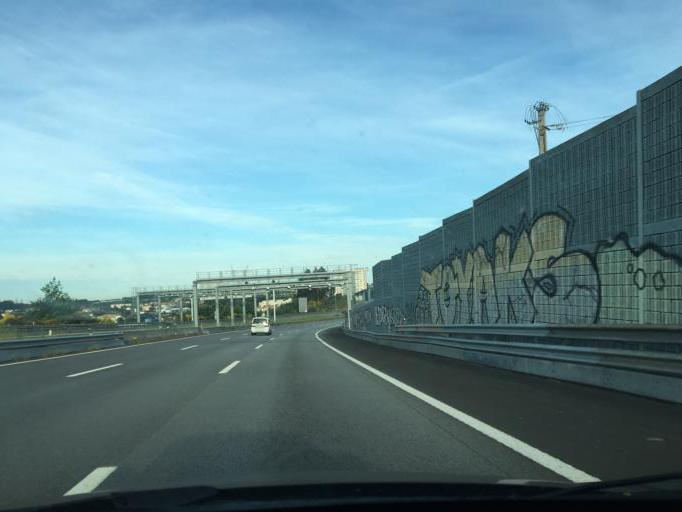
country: PT
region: Porto
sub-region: Maia
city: Maia
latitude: 41.2397
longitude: -8.6364
